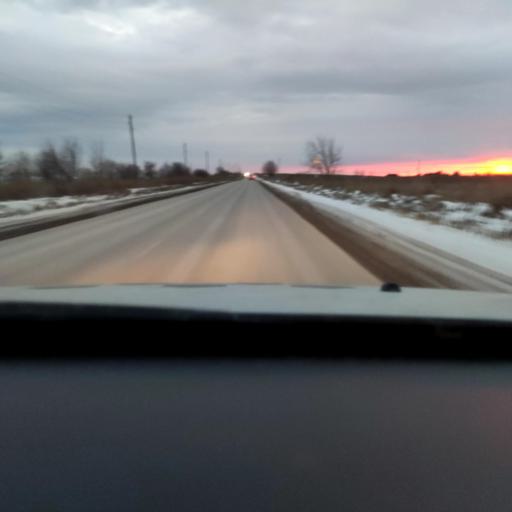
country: RU
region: Perm
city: Gamovo
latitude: 57.8892
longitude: 56.1090
